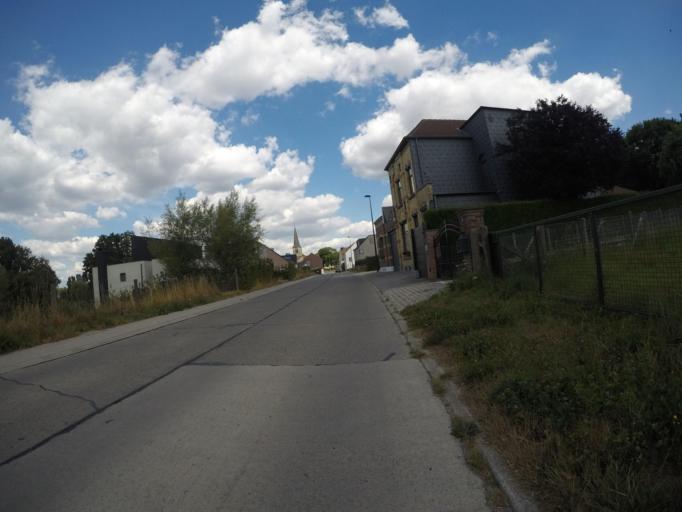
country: BE
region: Flanders
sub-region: Provincie Vlaams-Brabant
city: Ternat
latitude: 50.8469
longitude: 4.1351
